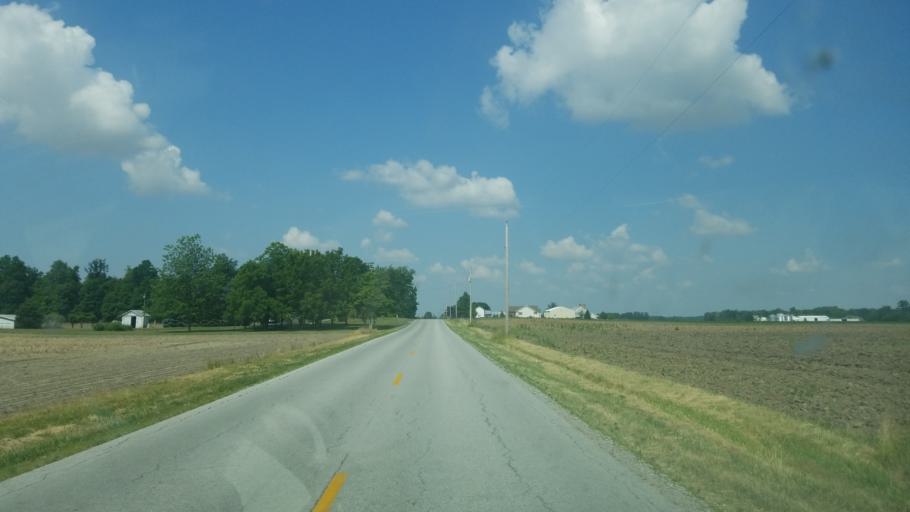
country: US
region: Ohio
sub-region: Auglaize County
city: Wapakoneta
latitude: 40.5704
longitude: -84.1324
